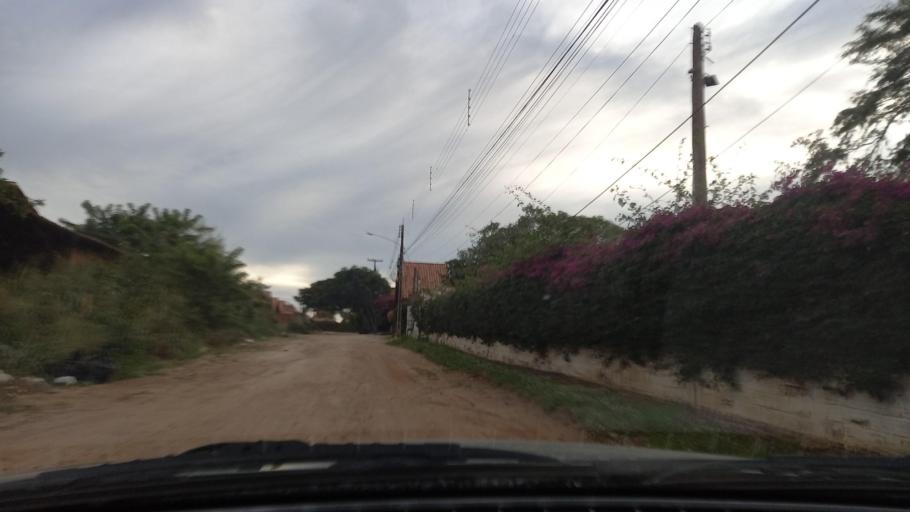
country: BR
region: Pernambuco
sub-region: Gravata
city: Gravata
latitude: -8.1965
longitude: -35.5866
